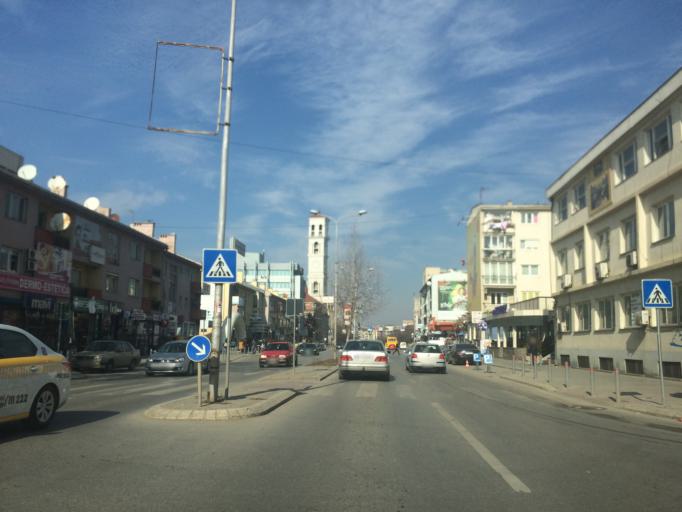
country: XK
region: Pristina
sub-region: Komuna e Prishtines
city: Pristina
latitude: 42.6538
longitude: 21.1592
